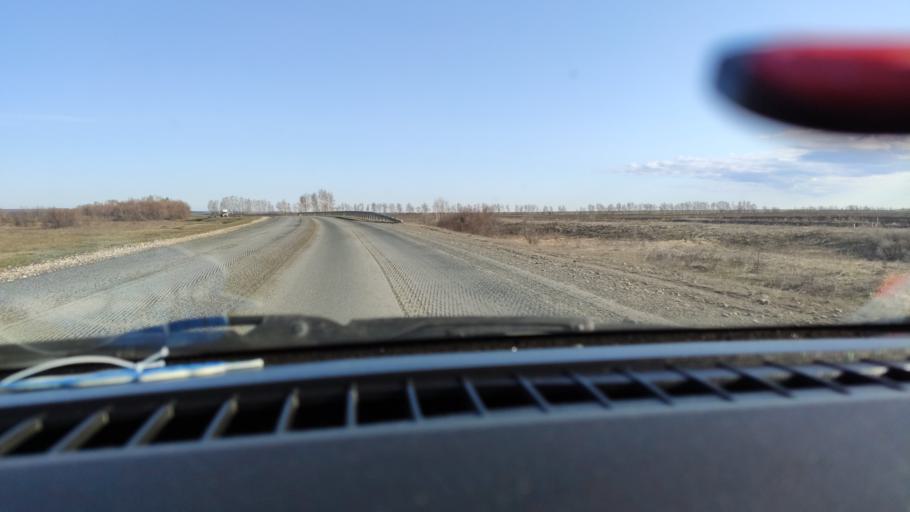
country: RU
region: Saratov
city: Dukhovnitskoye
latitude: 52.7140
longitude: 48.2663
